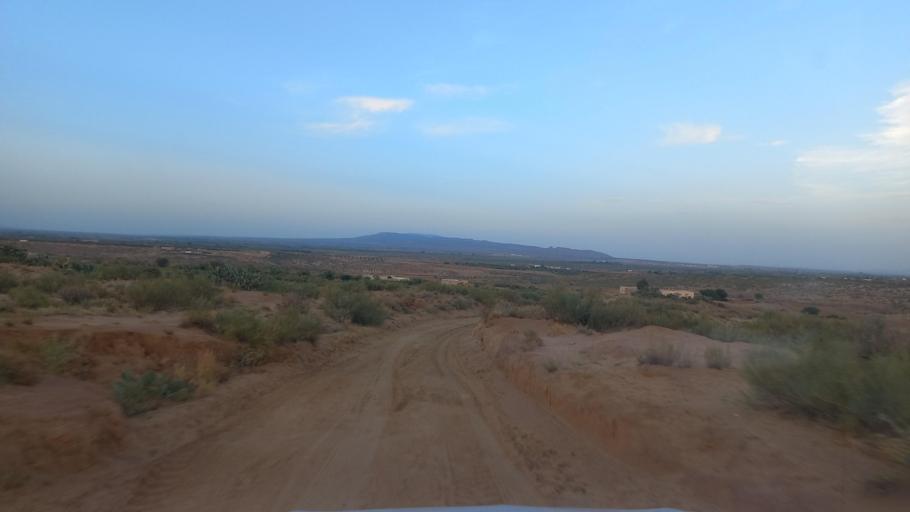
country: TN
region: Al Qasrayn
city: Kasserine
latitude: 35.1948
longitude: 9.0486
